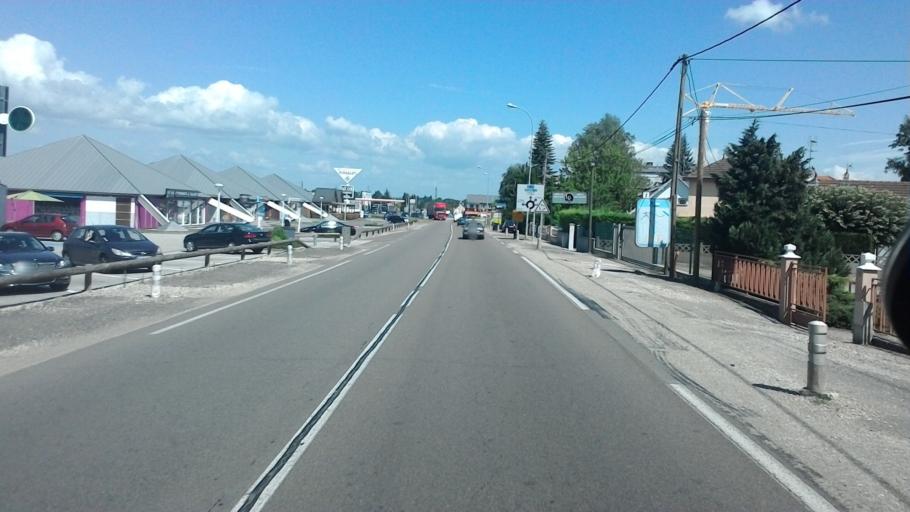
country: FR
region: Bourgogne
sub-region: Departement de Saone-et-Loire
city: Saint-Remy
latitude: 46.7520
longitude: 4.8483
